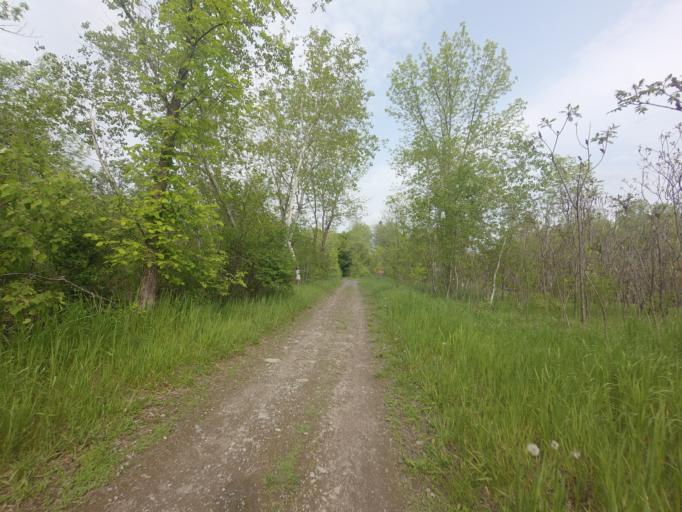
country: CA
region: Ontario
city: Kingston
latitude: 44.4093
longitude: -76.6154
